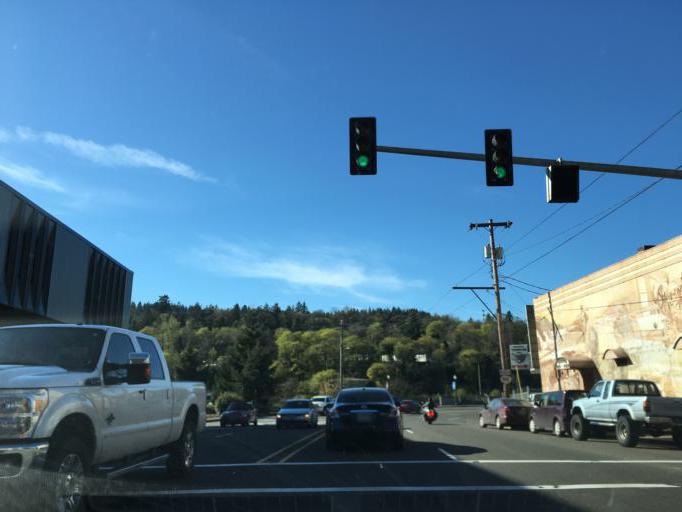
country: US
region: Oregon
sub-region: Clackamas County
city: Oregon City
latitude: 45.3566
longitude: -122.6101
